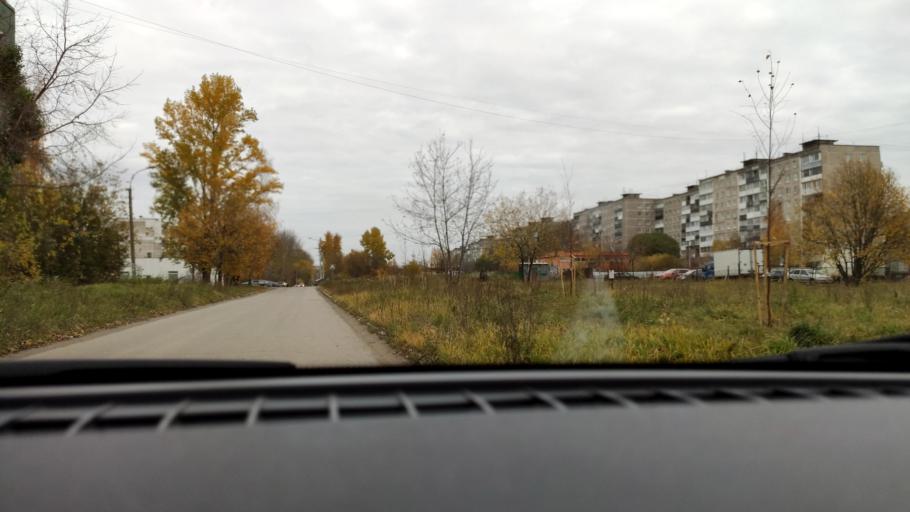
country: RU
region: Perm
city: Perm
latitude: 58.0588
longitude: 56.3476
